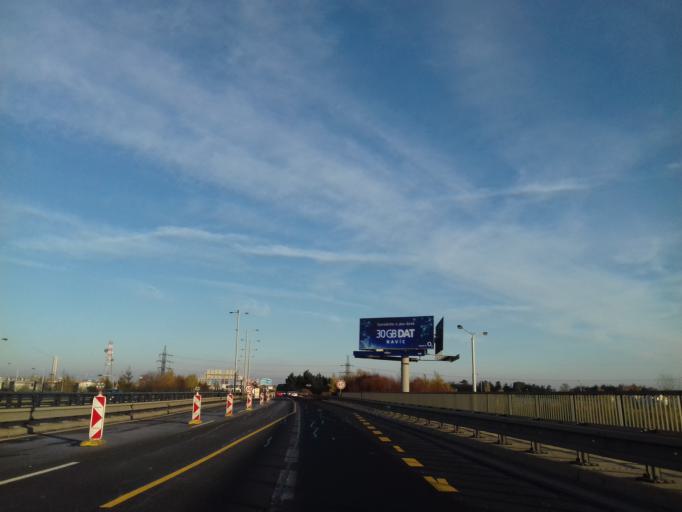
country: CZ
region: Central Bohemia
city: Hostivice
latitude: 50.0490
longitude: 14.2733
